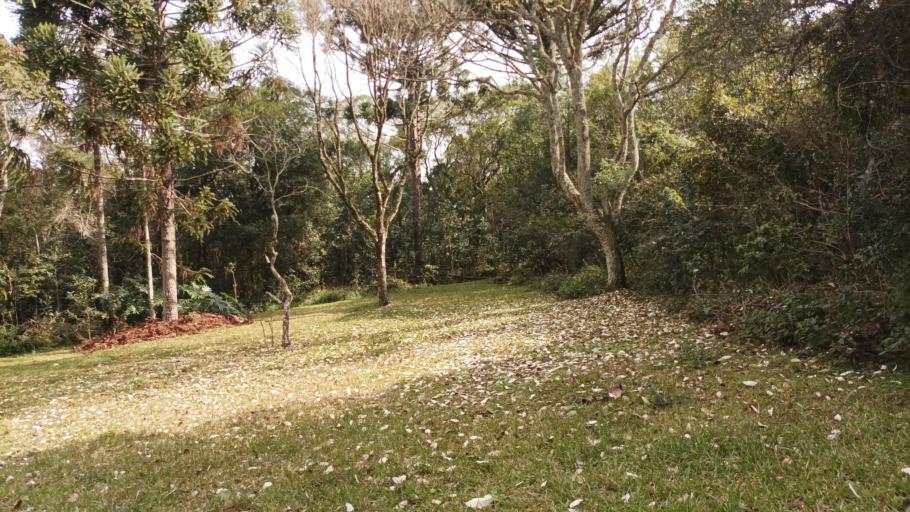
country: AR
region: Misiones
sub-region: Departamento de San Pedro
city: San Pedro
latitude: -26.6311
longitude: -54.1041
